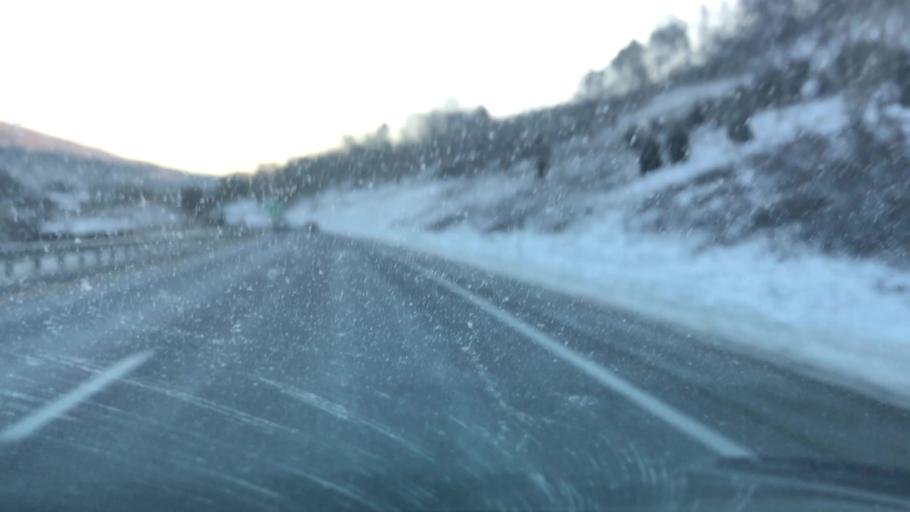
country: US
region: Virginia
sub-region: Montgomery County
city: Shawsville
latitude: 37.2279
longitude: -80.2432
